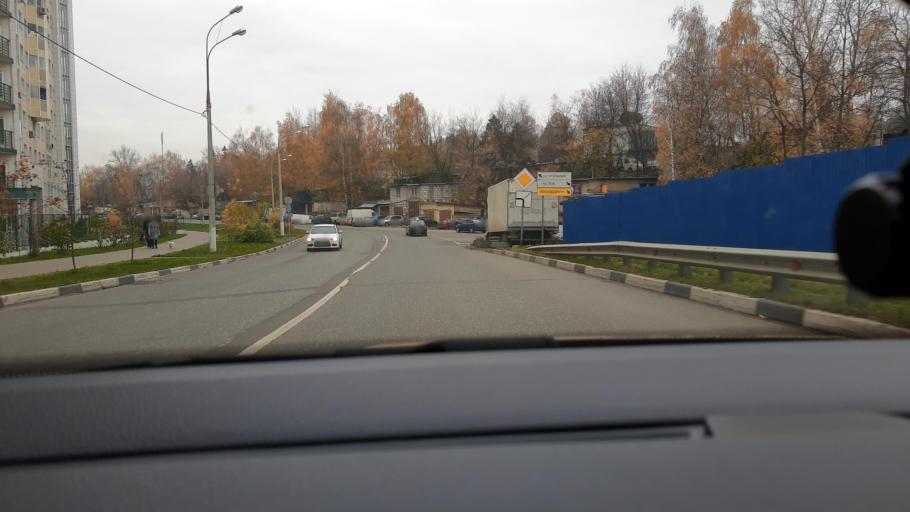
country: RU
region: Moskovskaya
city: Cherkizovo
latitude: 55.9439
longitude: 37.7739
